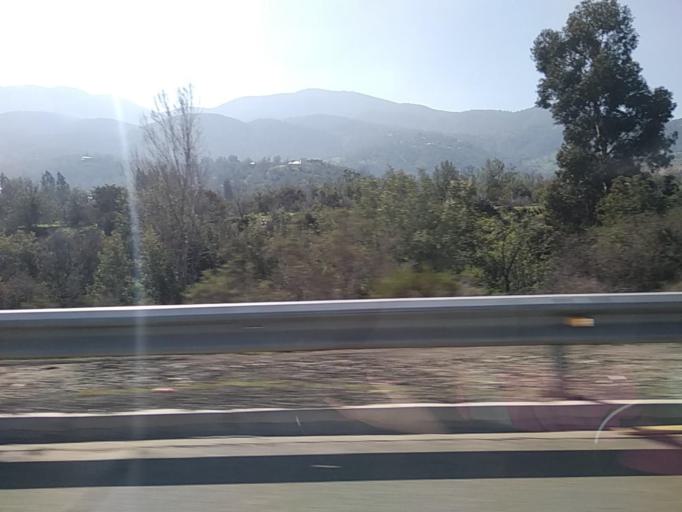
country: CL
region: Santiago Metropolitan
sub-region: Provincia de Melipilla
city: Melipilla
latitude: -33.4026
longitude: -71.2182
